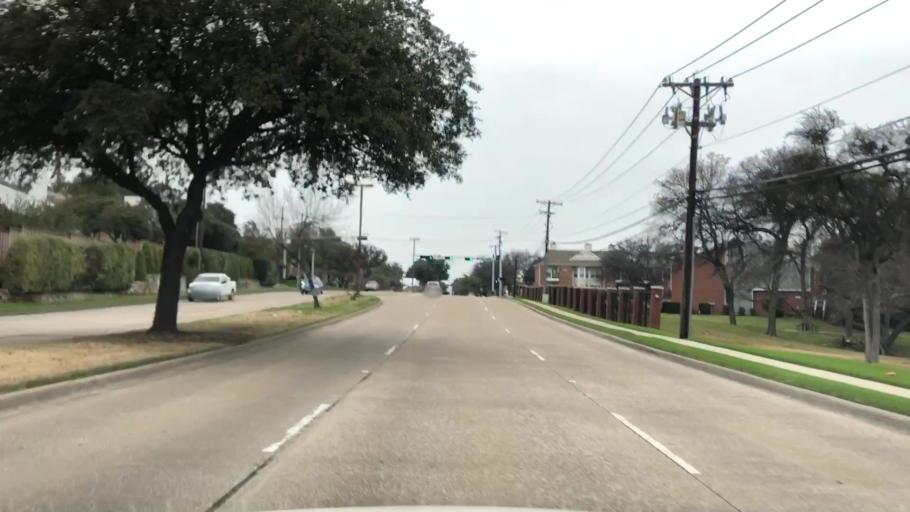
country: US
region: Texas
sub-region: Dallas County
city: Addison
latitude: 32.9653
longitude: -96.8535
